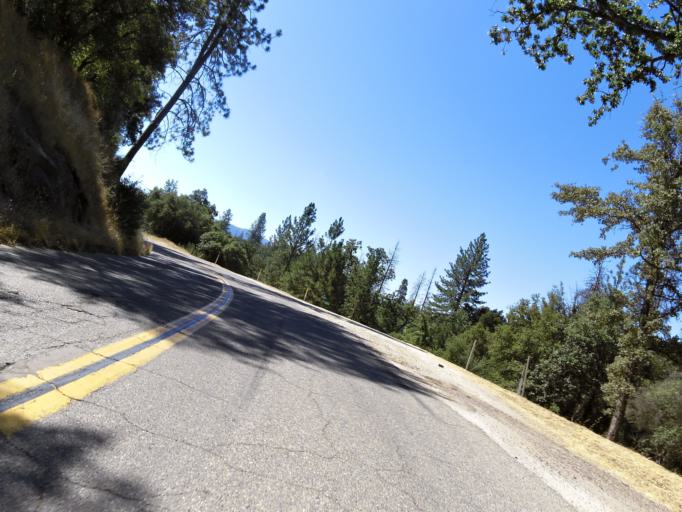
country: US
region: California
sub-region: Fresno County
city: Auberry
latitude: 37.1940
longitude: -119.4679
